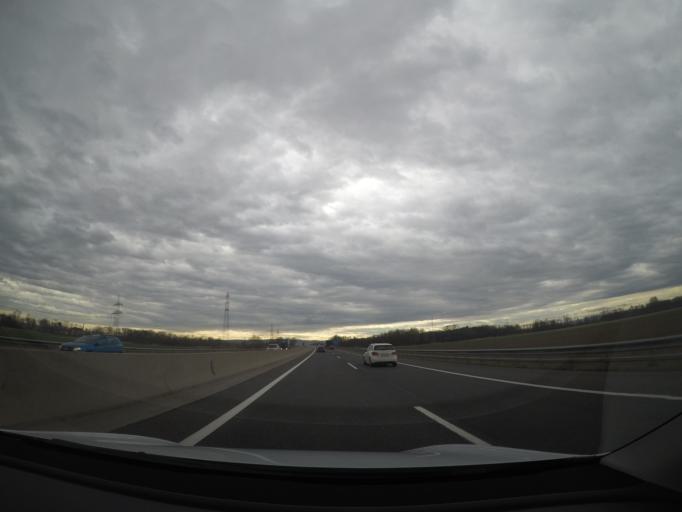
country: AT
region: Lower Austria
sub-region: Politischer Bezirk Baden
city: Ebreichsdorf
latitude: 47.9378
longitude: 16.3784
